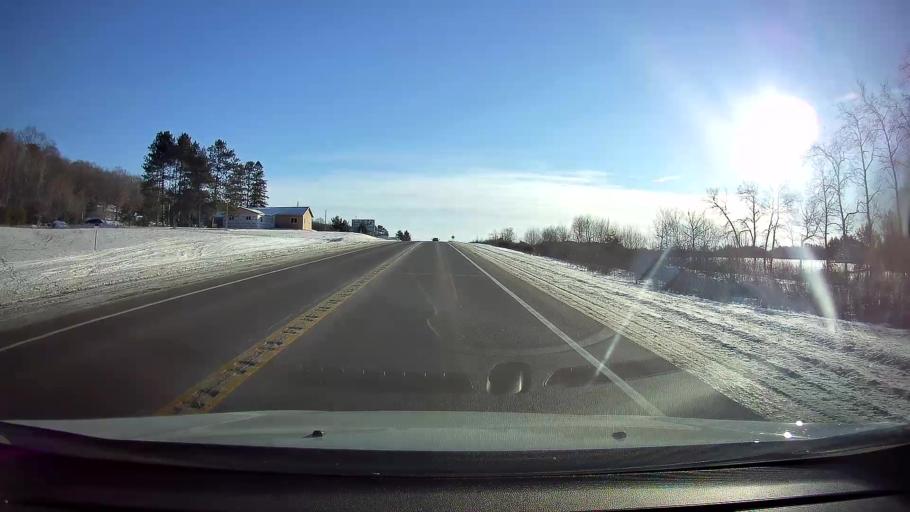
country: US
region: Wisconsin
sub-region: Sawyer County
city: Hayward
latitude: 45.9826
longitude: -91.5672
